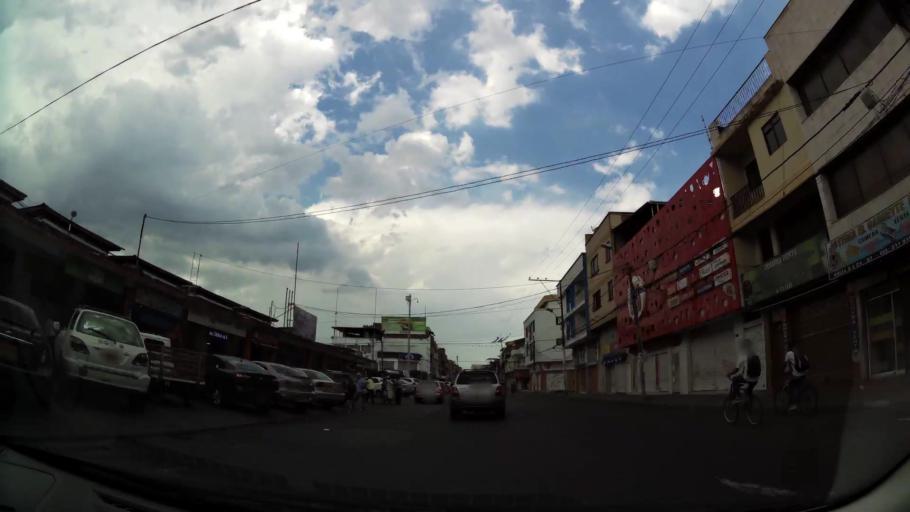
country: CO
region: Valle del Cauca
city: Cali
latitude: 3.4339
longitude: -76.5351
